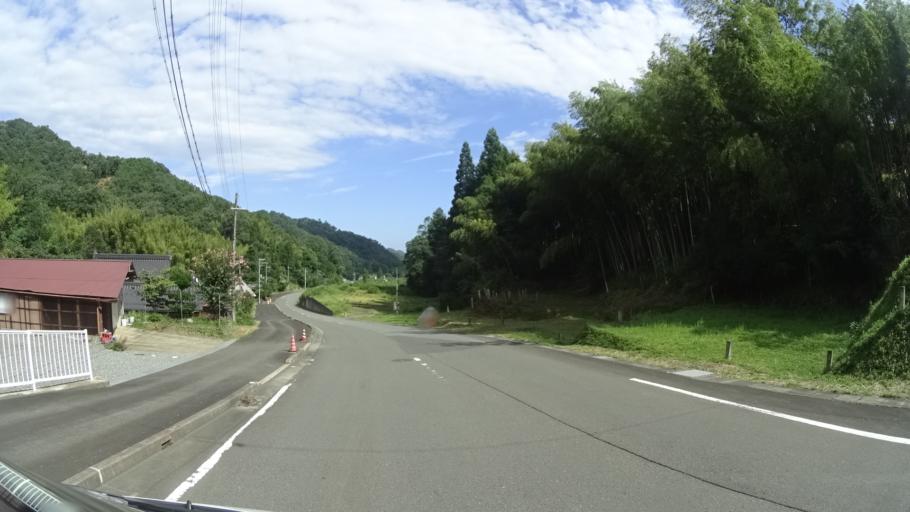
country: JP
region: Kyoto
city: Fukuchiyama
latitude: 35.3423
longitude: 135.1621
